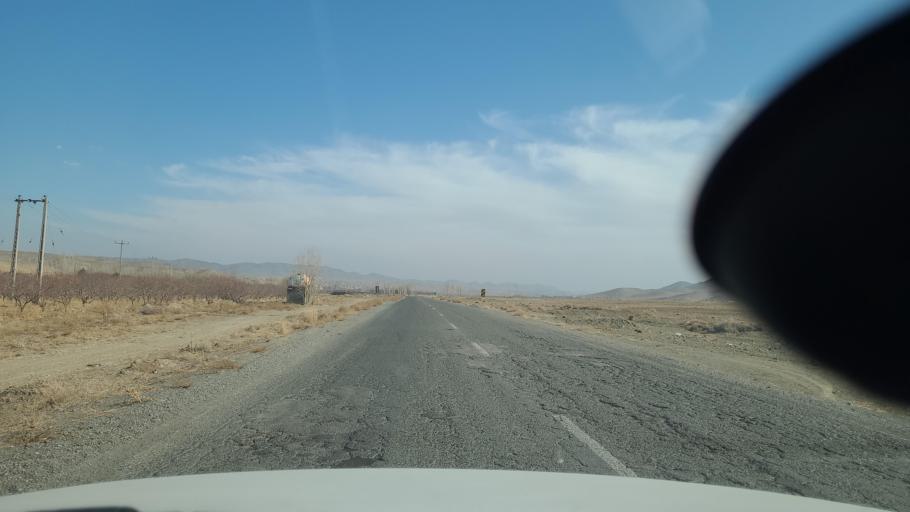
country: IR
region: Razavi Khorasan
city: Fariman
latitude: 35.5882
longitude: 59.6616
